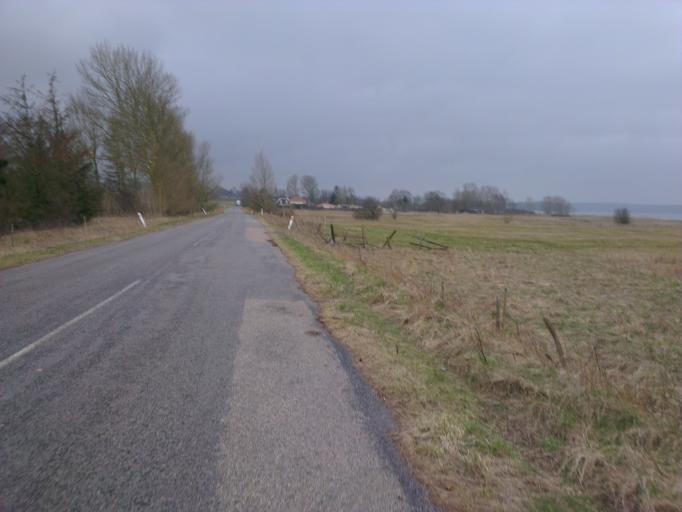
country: DK
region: Capital Region
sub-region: Frederikssund Kommune
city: Frederikssund
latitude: 55.8737
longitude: 12.0693
